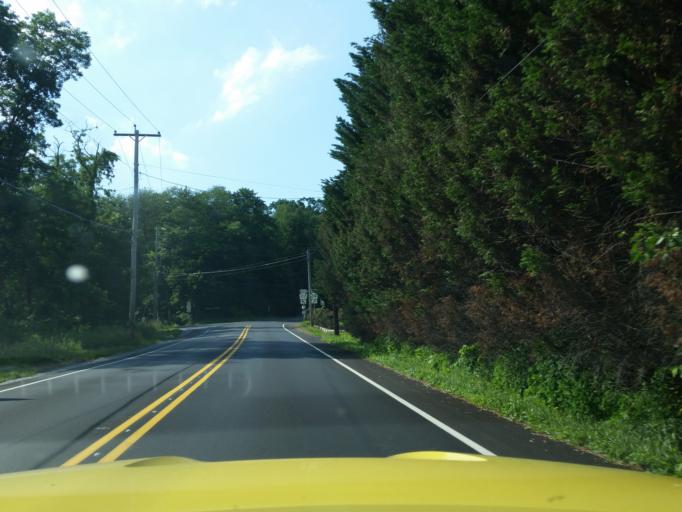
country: US
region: Pennsylvania
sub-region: Lebanon County
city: Campbelltown
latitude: 40.2455
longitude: -76.5173
